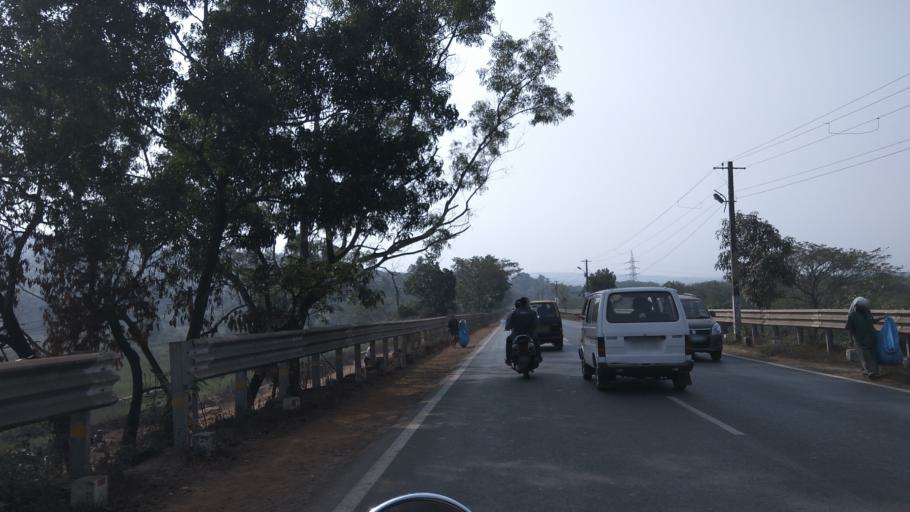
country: IN
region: Goa
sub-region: North Goa
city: Jua
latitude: 15.4886
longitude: 73.9582
